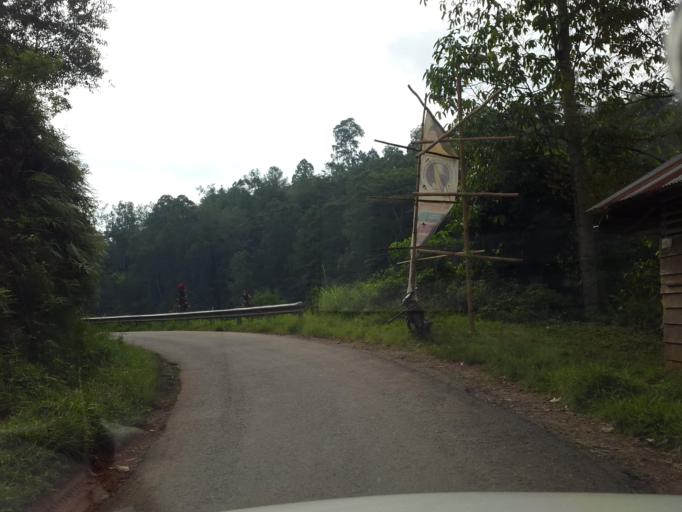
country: ID
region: South Sulawesi
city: Makale
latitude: -3.0306
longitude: 119.8489
